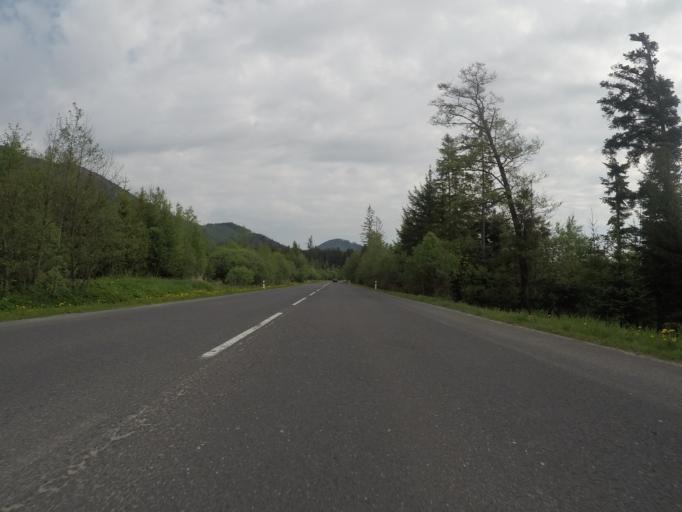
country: SK
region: Presovsky
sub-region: Okres Poprad
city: Zdiar
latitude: 49.2038
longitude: 20.3079
